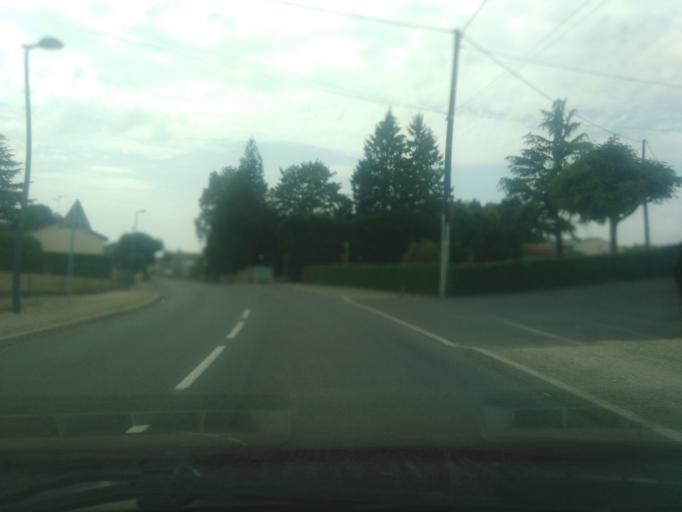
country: FR
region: Poitou-Charentes
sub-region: Departement des Deux-Sevres
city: Moncoutant
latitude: 46.6437
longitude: -0.5966
